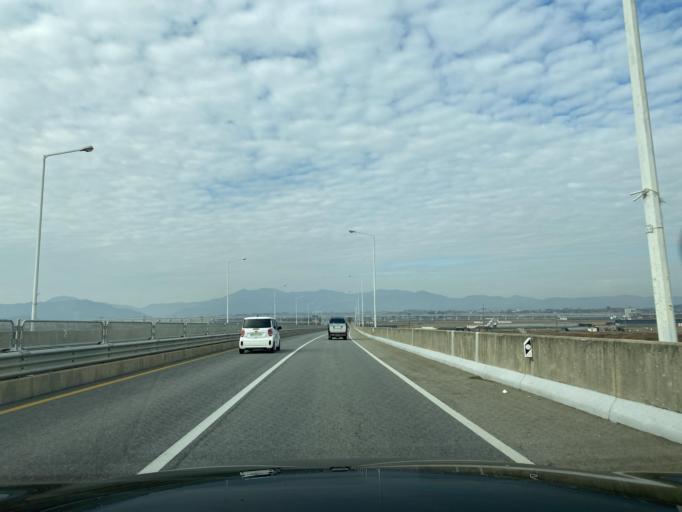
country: KR
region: Chungcheongnam-do
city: Yesan
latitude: 36.6912
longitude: 126.7378
